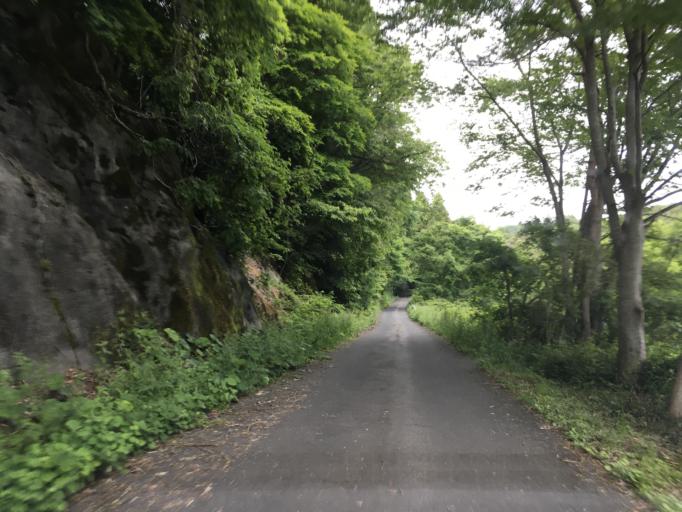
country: JP
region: Iwate
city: Mizusawa
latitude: 39.1223
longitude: 141.2616
